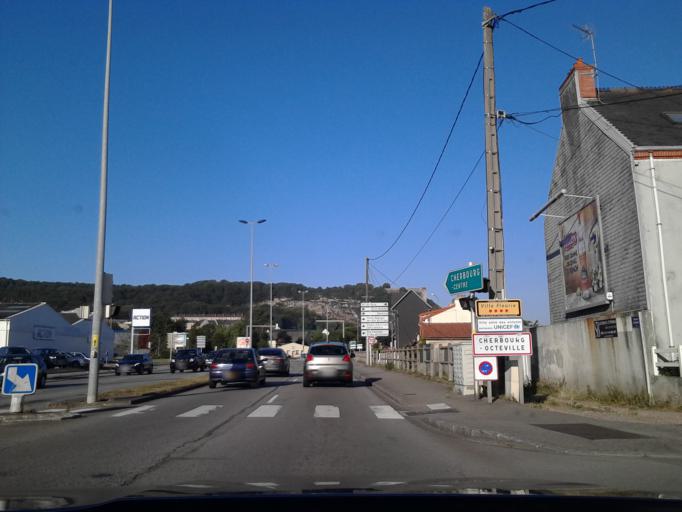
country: FR
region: Lower Normandy
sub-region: Departement de la Manche
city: Cherbourg-Octeville
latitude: 49.6352
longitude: -1.6010
